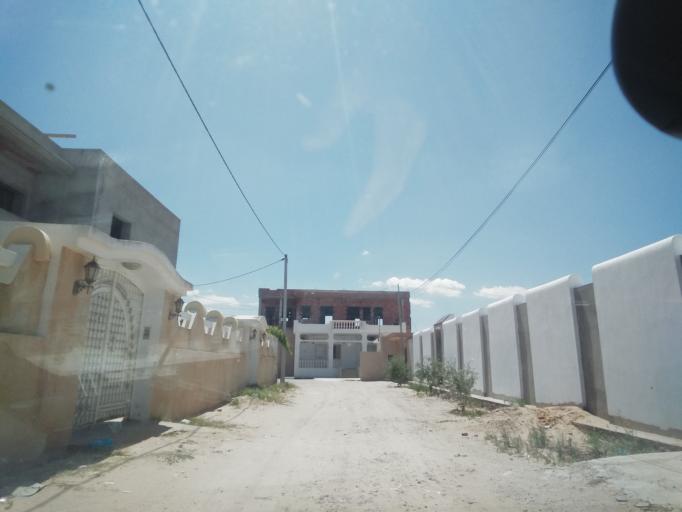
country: TN
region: Safaqis
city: Al Qarmadah
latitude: 34.8253
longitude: 10.7650
